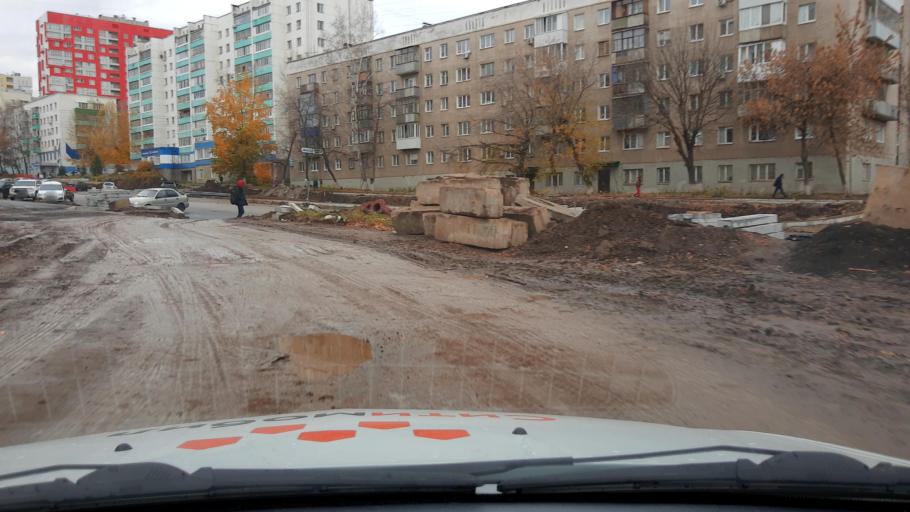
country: RU
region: Bashkortostan
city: Ufa
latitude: 54.7434
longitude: 55.9971
